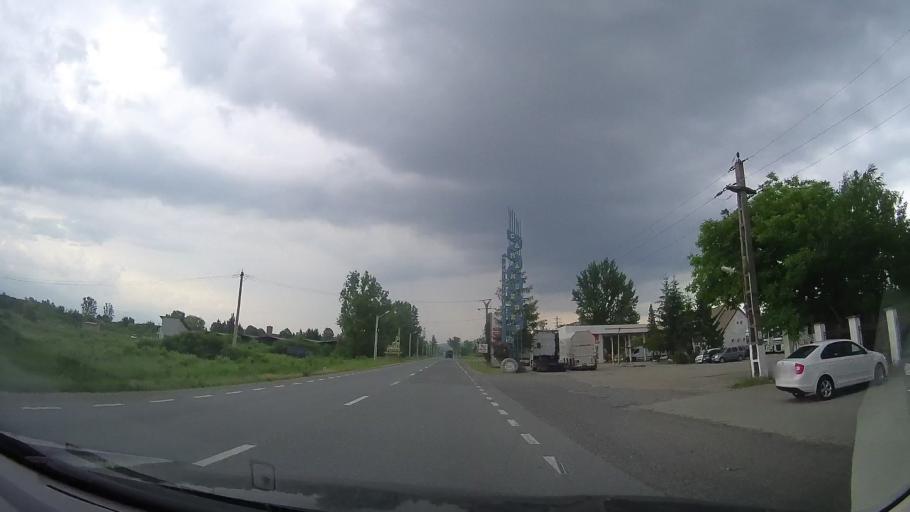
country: RO
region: Caras-Severin
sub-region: Municipiul Caransebes
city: Caransebes
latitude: 45.4373
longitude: 22.1933
